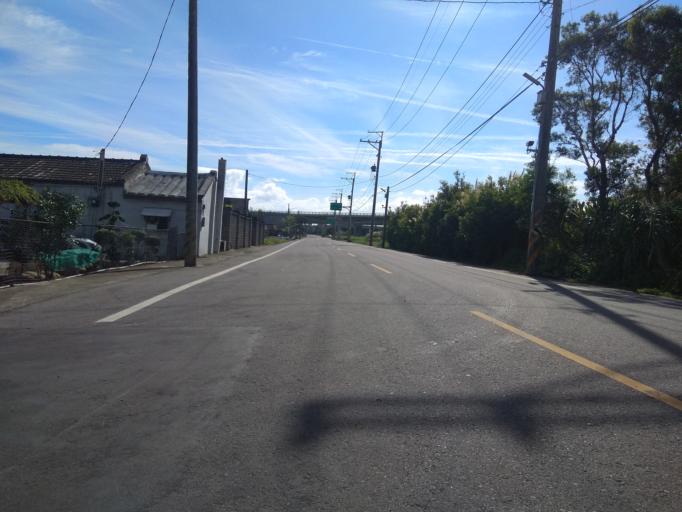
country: TW
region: Taiwan
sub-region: Hsinchu
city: Zhubei
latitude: 25.0147
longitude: 121.0344
